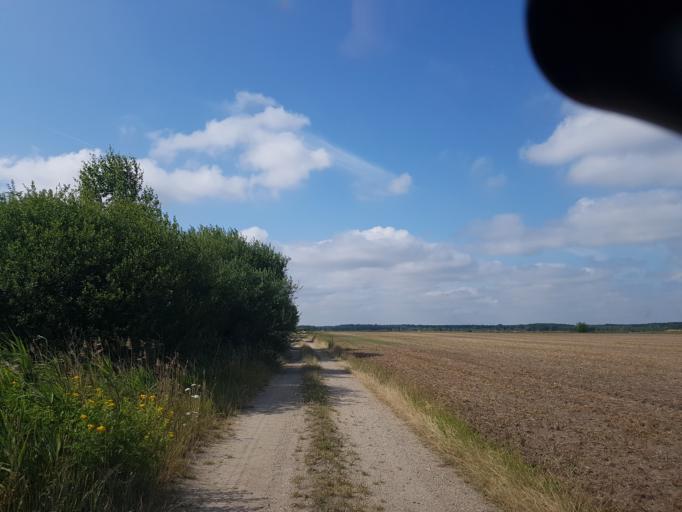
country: DE
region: Brandenburg
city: Schonborn
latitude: 51.5933
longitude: 13.5107
